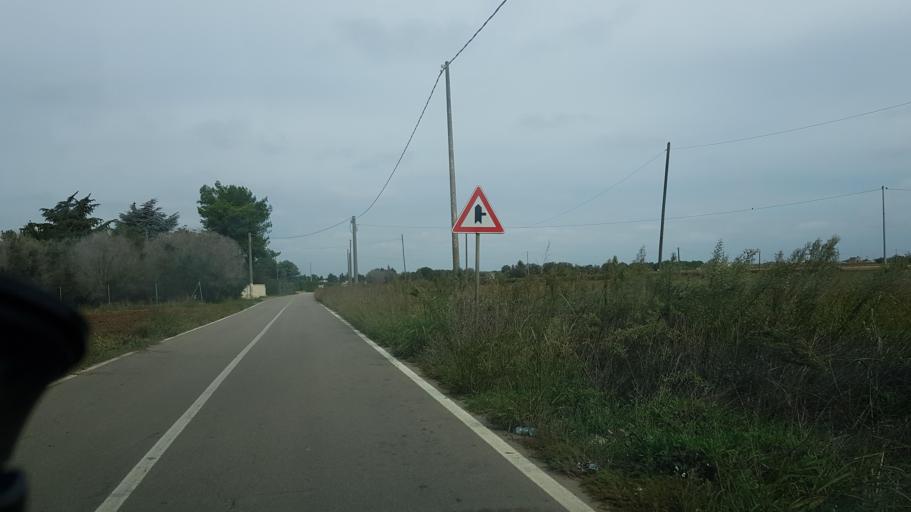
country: IT
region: Apulia
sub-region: Provincia di Lecce
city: Guagnano
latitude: 40.4087
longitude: 17.9496
